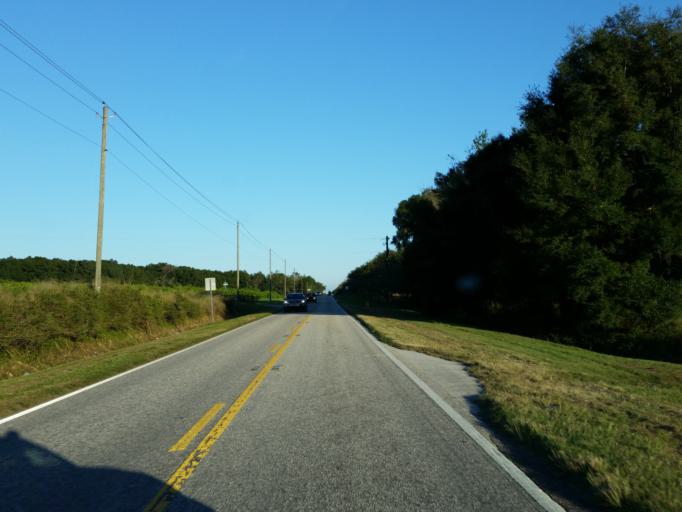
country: US
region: Florida
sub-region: Pasco County
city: Dade City North
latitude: 28.4163
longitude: -82.2627
